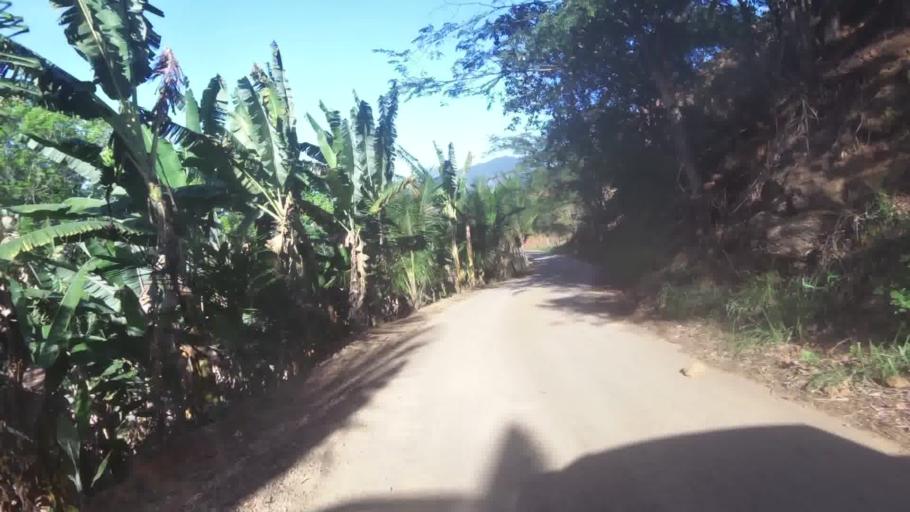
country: BR
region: Espirito Santo
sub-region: Iconha
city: Iconha
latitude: -20.7401
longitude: -40.7940
